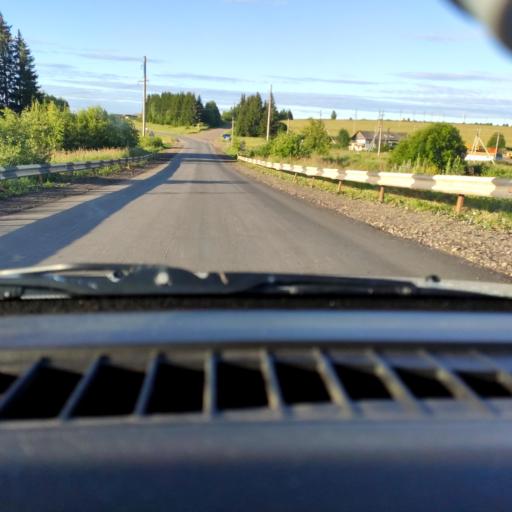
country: RU
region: Perm
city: Uinskoye
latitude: 57.1105
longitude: 56.5315
